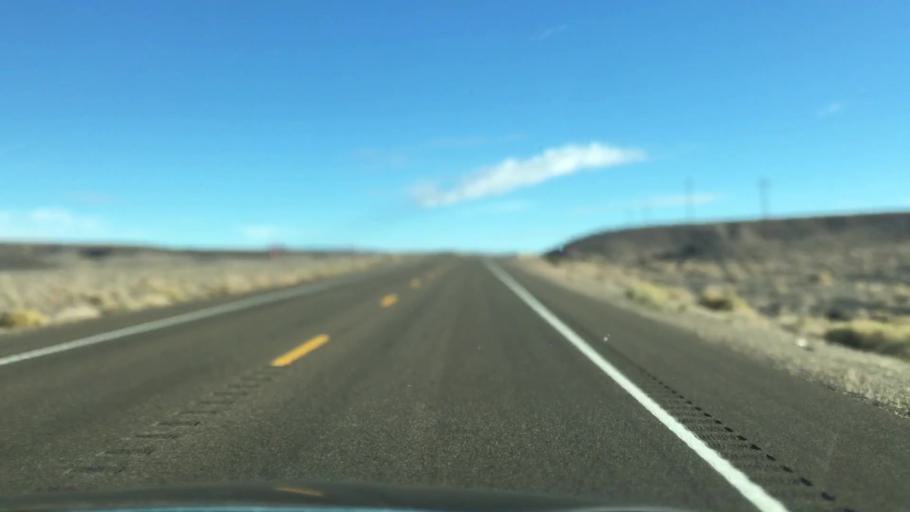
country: US
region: Nevada
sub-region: Mineral County
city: Hawthorne
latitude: 38.2316
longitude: -118.0210
